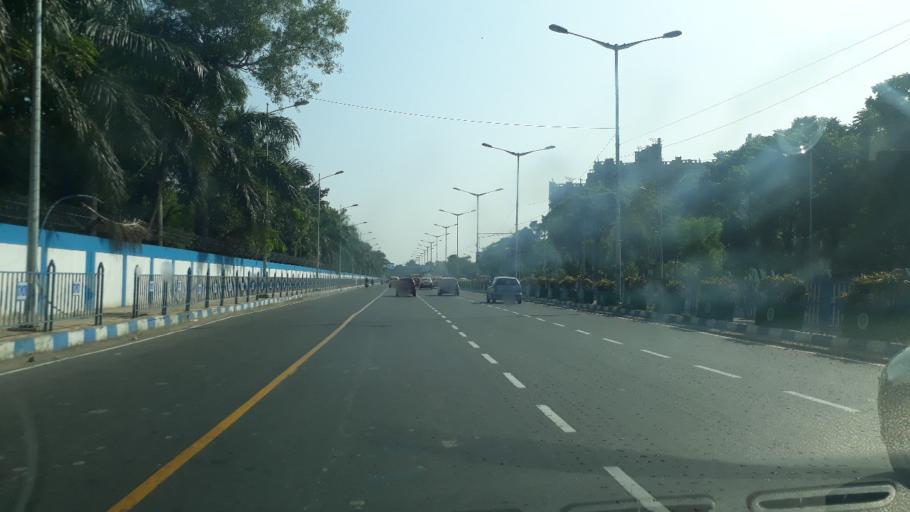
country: IN
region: West Bengal
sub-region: Kolkata
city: Kolkata
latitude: 22.5664
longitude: 88.4064
